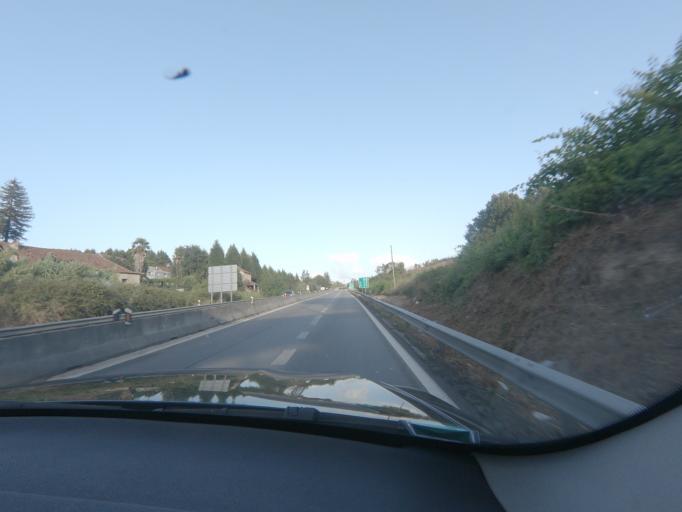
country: PT
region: Viseu
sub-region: Santa Comba Dao
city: Santa Comba Dao
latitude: 40.3875
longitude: -8.1252
